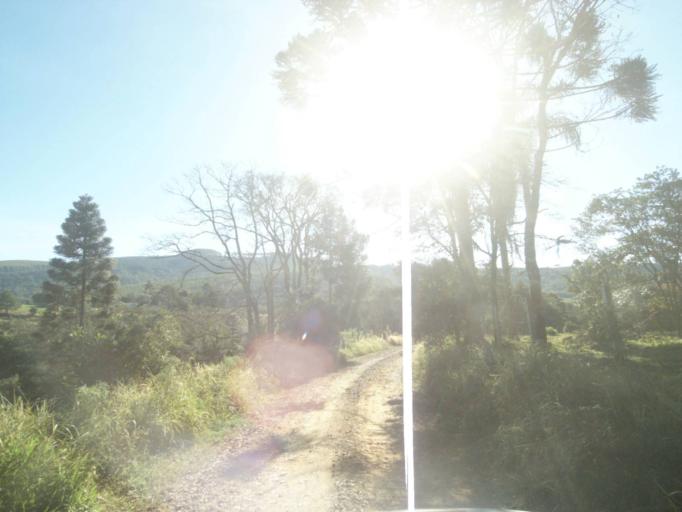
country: BR
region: Parana
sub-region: Tibagi
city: Tibagi
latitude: -24.5522
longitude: -50.5180
